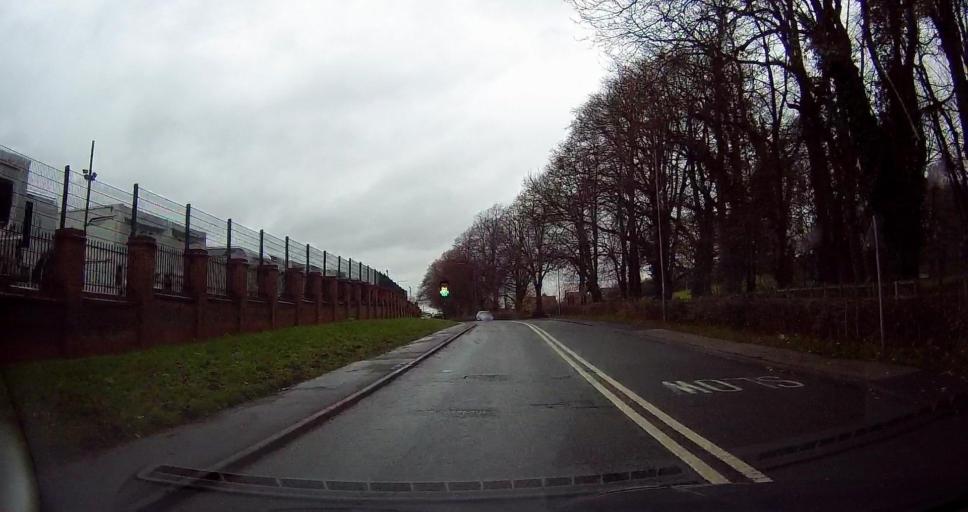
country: GB
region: England
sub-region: Nottinghamshire
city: Kimberley
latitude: 52.9987
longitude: -1.2637
